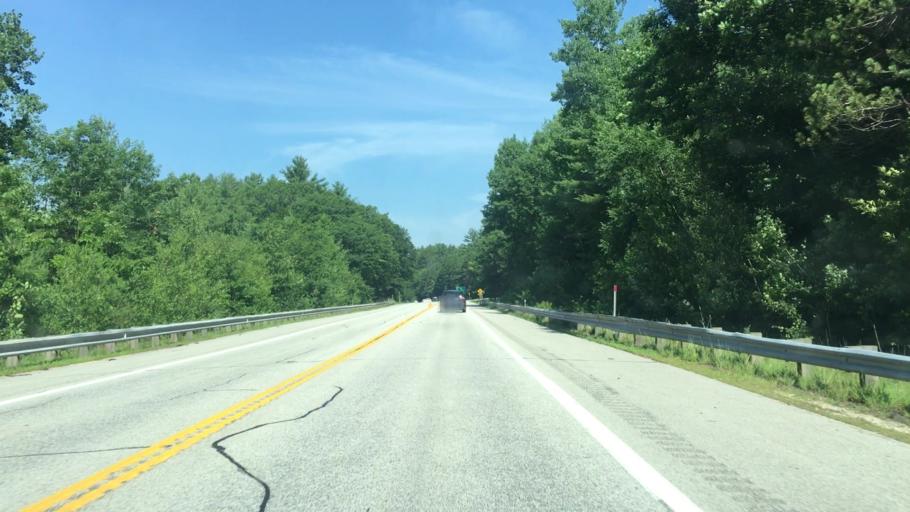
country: US
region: New Hampshire
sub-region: Merrimack County
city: Henniker
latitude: 43.1883
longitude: -71.8079
